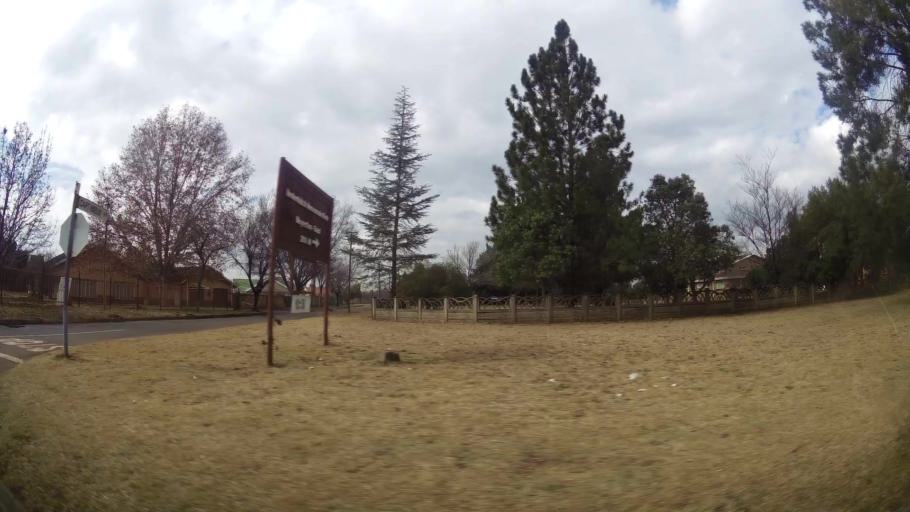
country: ZA
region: Gauteng
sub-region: Sedibeng District Municipality
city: Meyerton
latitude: -26.5914
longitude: 27.9990
